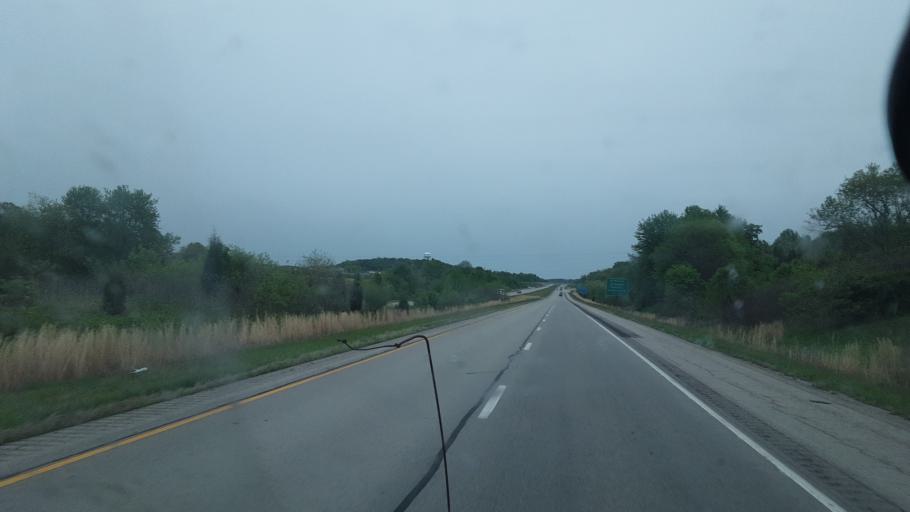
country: US
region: Indiana
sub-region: Dubois County
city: Ferdinand
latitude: 38.2063
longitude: -86.8825
